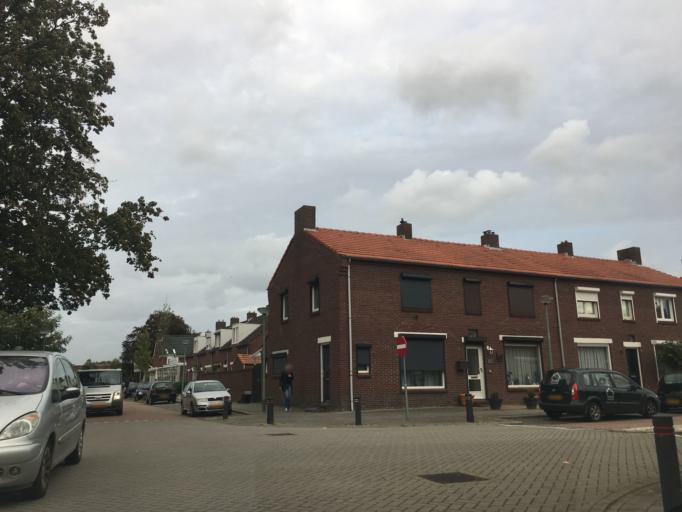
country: NL
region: Limburg
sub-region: Gemeente Roermond
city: Roermond
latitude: 51.1766
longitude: 6.0003
